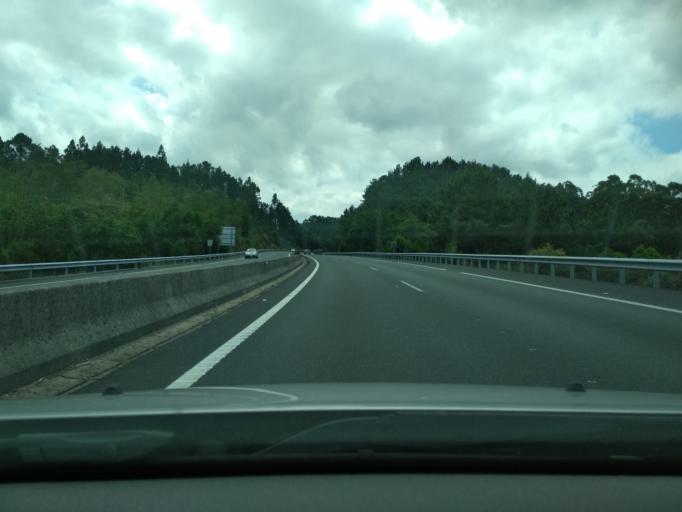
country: ES
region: Galicia
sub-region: Provincia de Pontevedra
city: Portas
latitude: 42.5817
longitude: -8.6753
